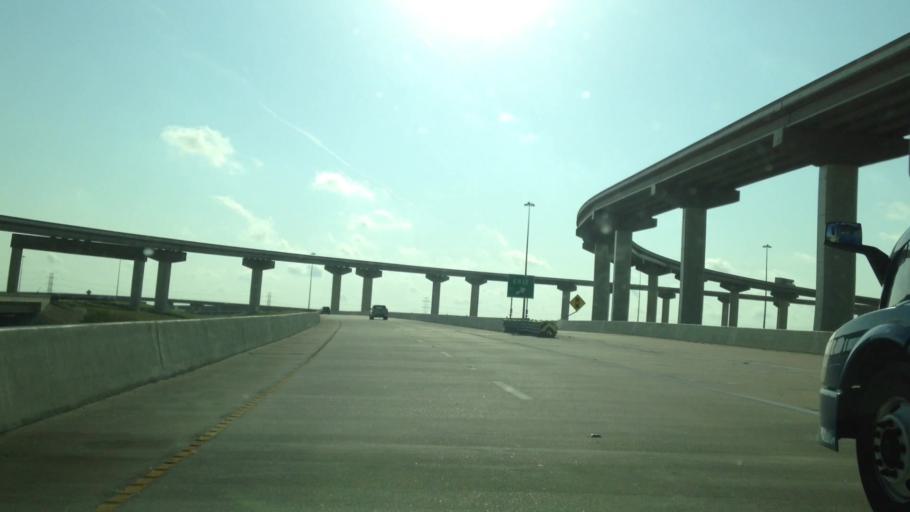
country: US
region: Texas
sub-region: Travis County
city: Onion Creek
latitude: 30.0804
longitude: -97.6974
